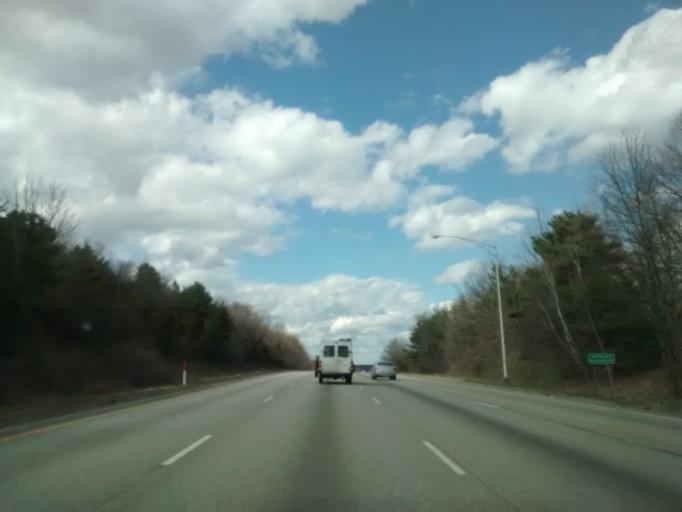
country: US
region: Massachusetts
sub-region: Worcester County
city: Southborough
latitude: 42.2921
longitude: -71.5661
